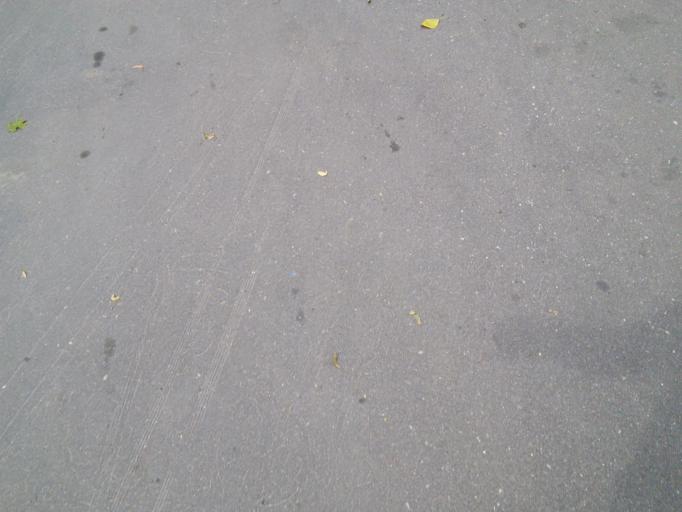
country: RU
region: Moskovskaya
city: Bogorodskoye
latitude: 55.7925
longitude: 37.7266
